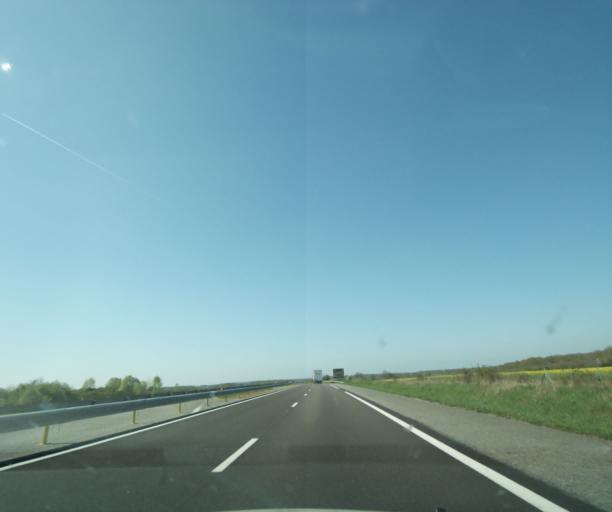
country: FR
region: Centre
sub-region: Departement du Loiret
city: Briare
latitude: 47.6296
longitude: 2.7880
